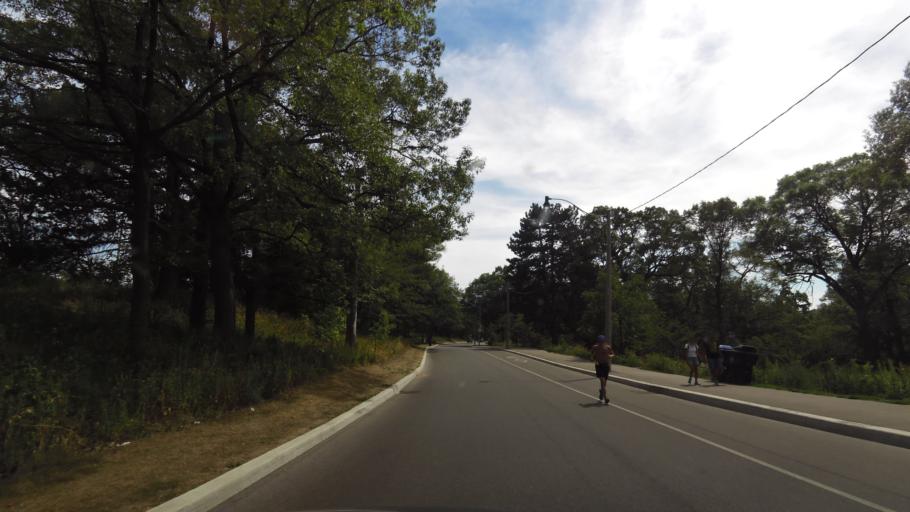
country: CA
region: Ontario
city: Toronto
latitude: 43.6495
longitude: -79.4681
